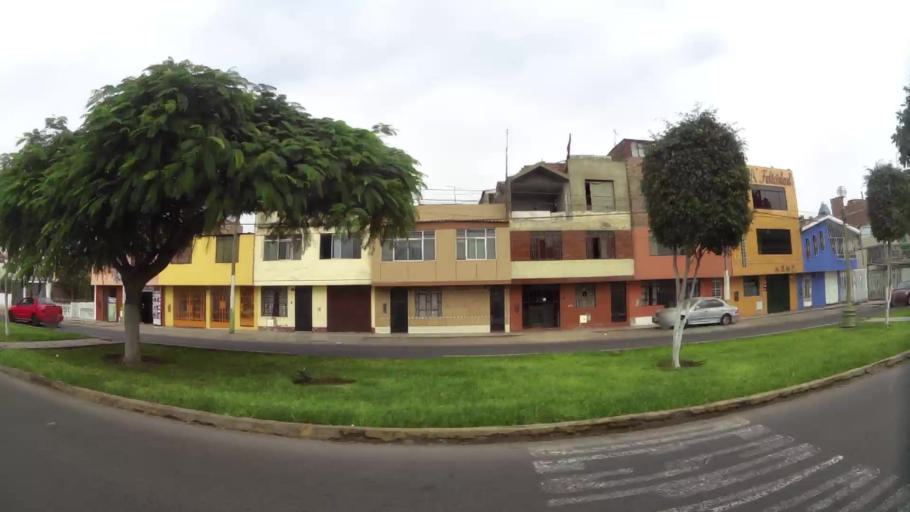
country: PE
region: Callao
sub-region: Callao
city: Callao
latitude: -12.0154
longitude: -77.0906
